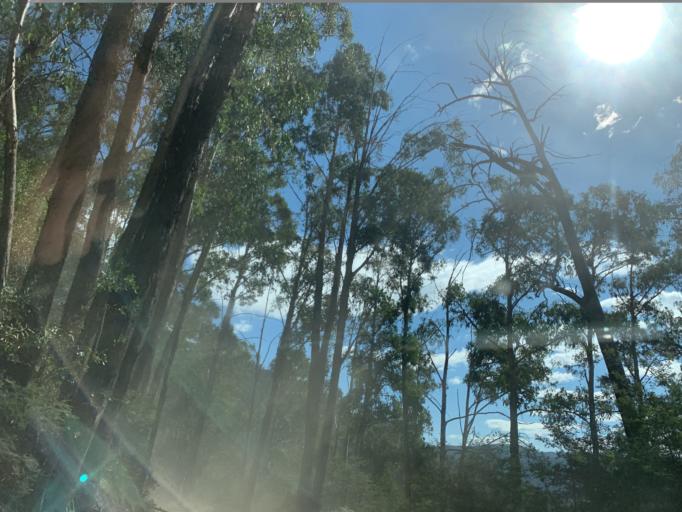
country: AU
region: Victoria
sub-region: Mansfield
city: Mansfield
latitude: -37.0978
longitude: 146.4856
